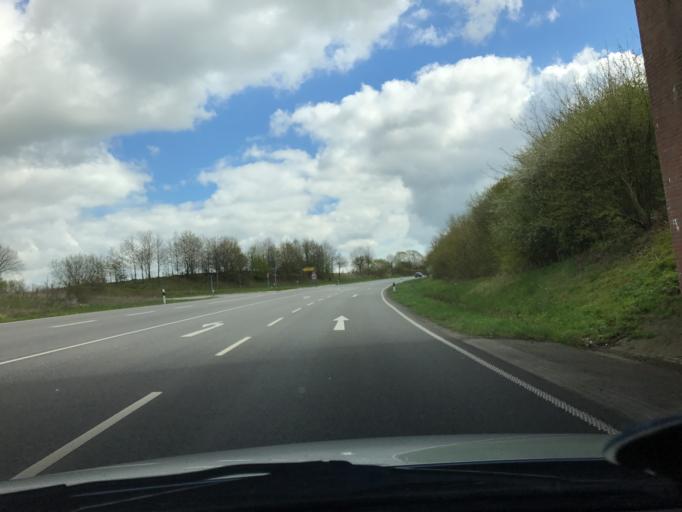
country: DE
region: Schleswig-Holstein
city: Eutin
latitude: 54.1193
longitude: 10.6382
